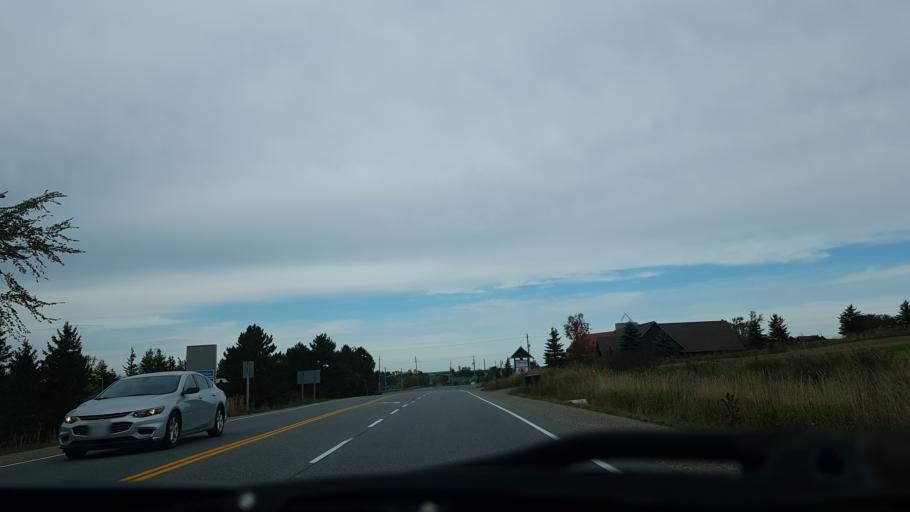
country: CA
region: Ontario
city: Shelburne
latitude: 44.1135
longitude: -80.0265
